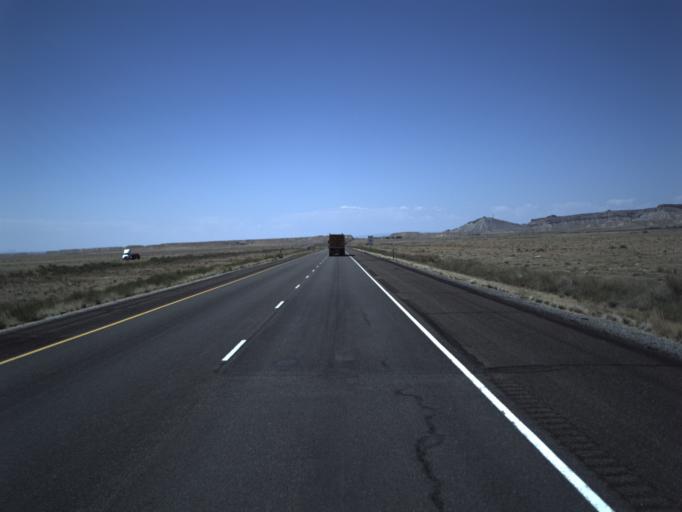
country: US
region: Utah
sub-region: Grand County
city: Moab
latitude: 38.9526
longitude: -109.7667
